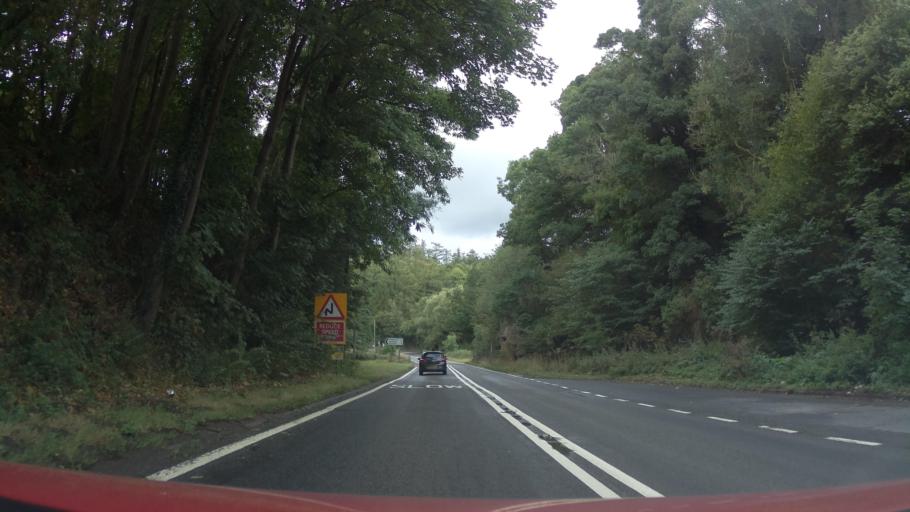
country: GB
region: England
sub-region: Shropshire
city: Bridgnorth
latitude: 52.5608
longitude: -2.3940
